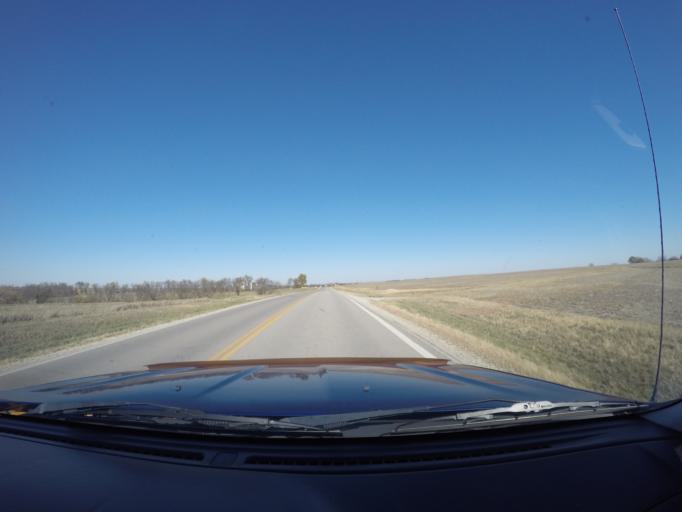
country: US
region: Kansas
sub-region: Marshall County
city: Marysville
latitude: 39.8504
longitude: -96.4170
